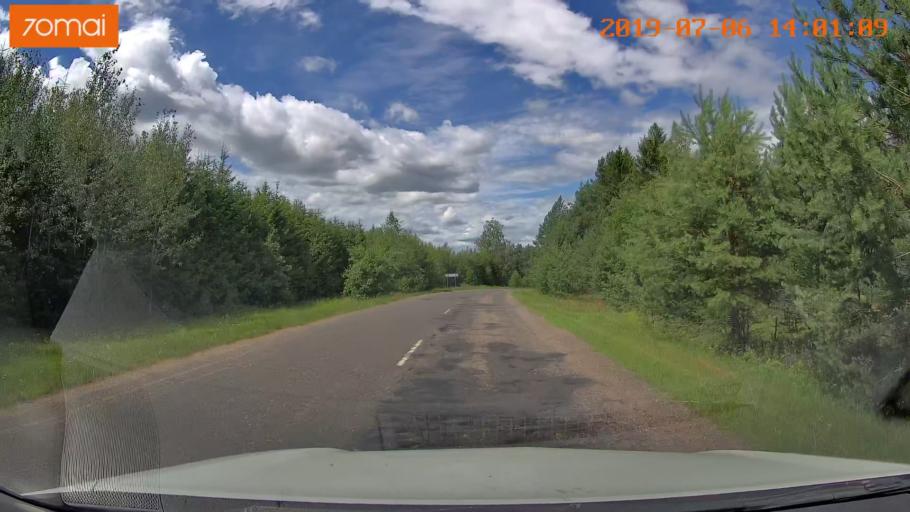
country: BY
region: Minsk
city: Ivyanyets
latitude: 53.8051
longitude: 26.8152
